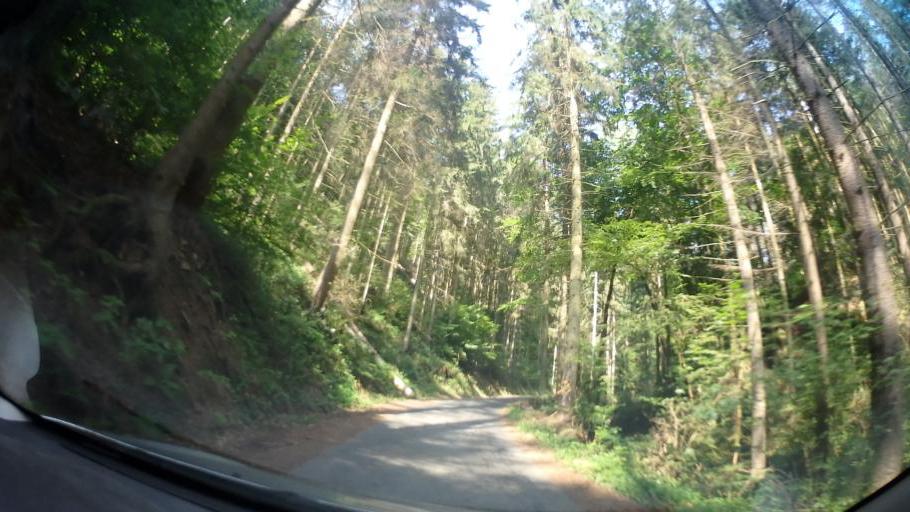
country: CZ
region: South Moravian
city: Olesnice
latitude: 49.5358
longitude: 16.3534
